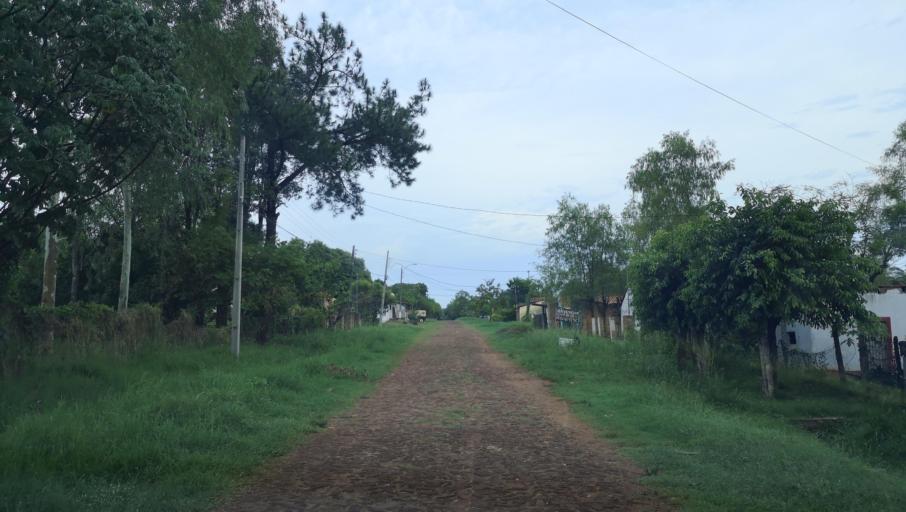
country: PY
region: Misiones
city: Santa Maria
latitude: -26.8837
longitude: -57.0194
